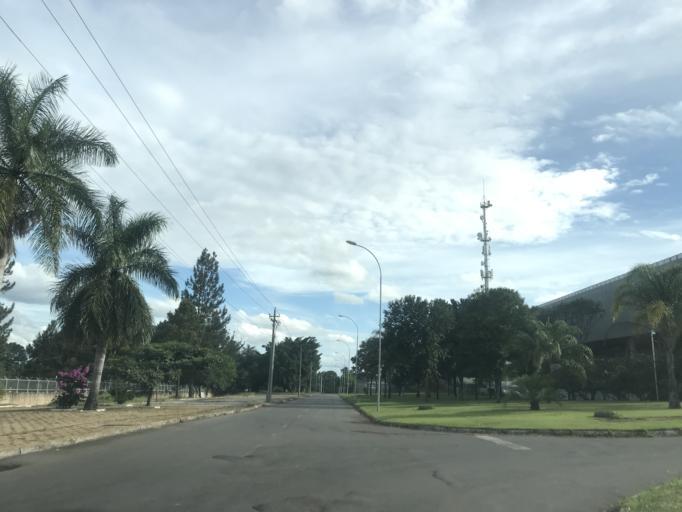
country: BR
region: Federal District
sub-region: Brasilia
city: Brasilia
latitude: -15.8159
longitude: -47.8869
